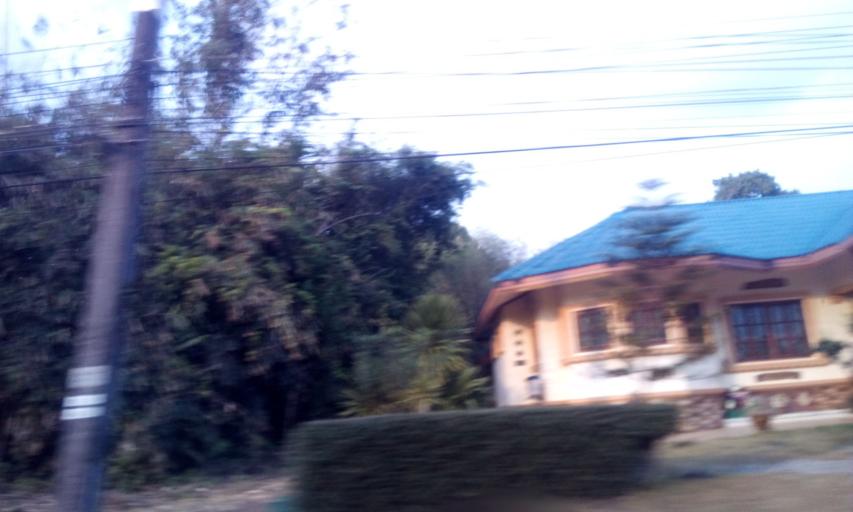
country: TH
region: Trat
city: Laem Ngop
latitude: 12.2517
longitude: 102.2910
